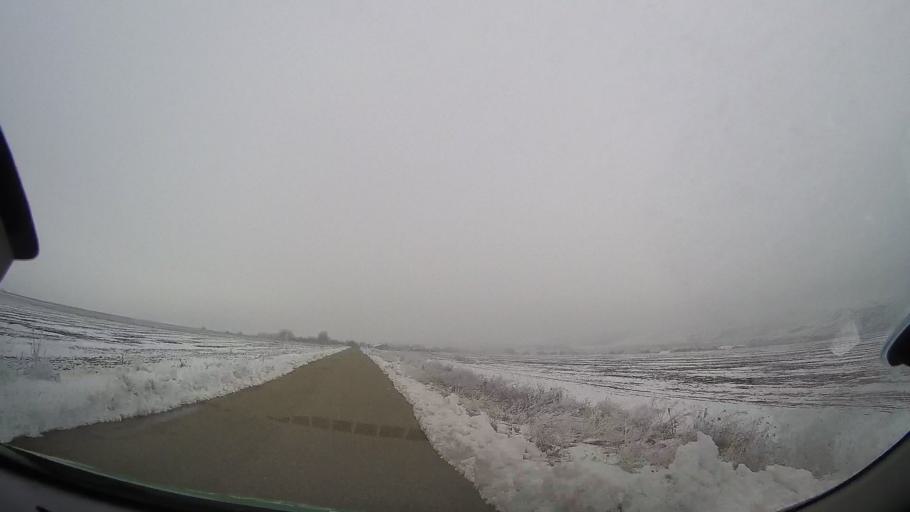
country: RO
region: Vaslui
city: Coroiesti
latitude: 46.2383
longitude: 27.4783
